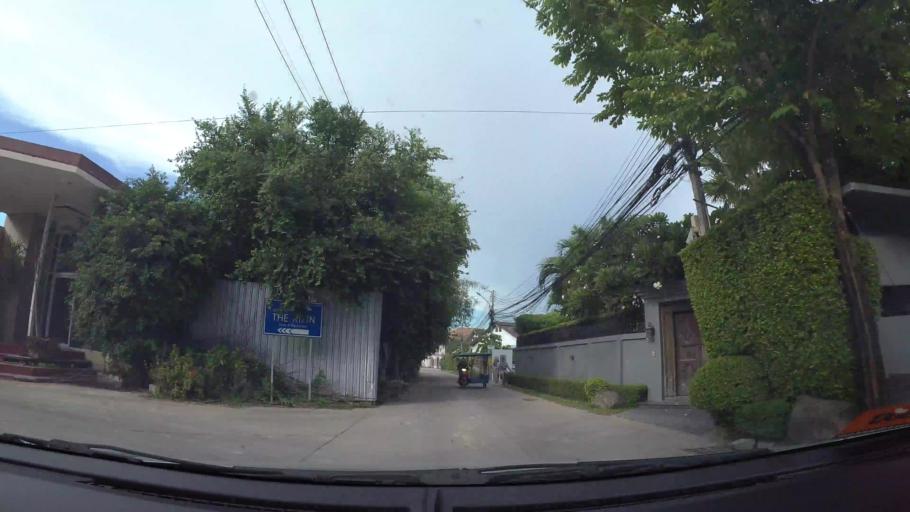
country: TH
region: Chon Buri
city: Phatthaya
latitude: 12.9110
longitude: 100.8738
